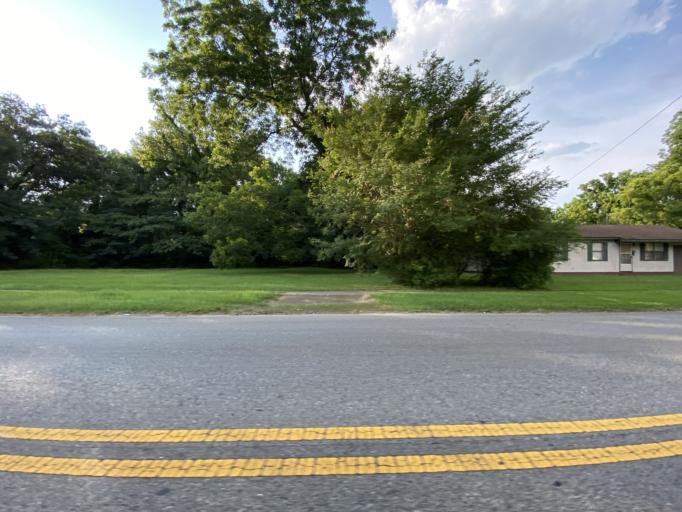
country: US
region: Alabama
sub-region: Morgan County
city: Hartselle
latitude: 34.4458
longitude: -86.9274
